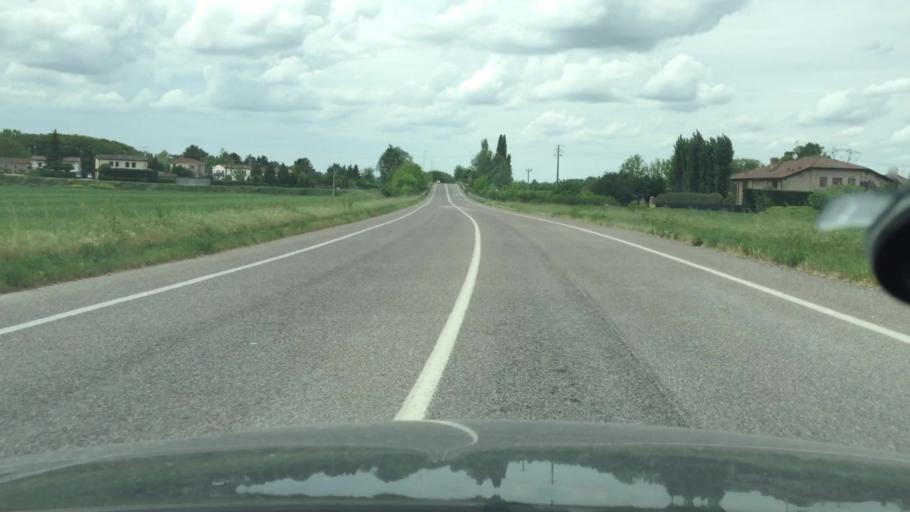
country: IT
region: Emilia-Romagna
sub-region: Provincia di Ferrara
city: Cona
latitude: 44.8100
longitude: 11.7169
